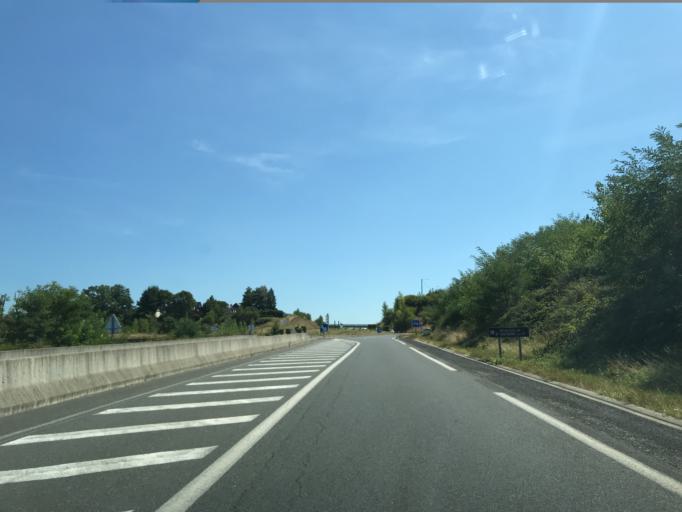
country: FR
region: Limousin
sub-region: Departement de la Correze
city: Ussac
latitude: 45.1954
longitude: 1.5394
